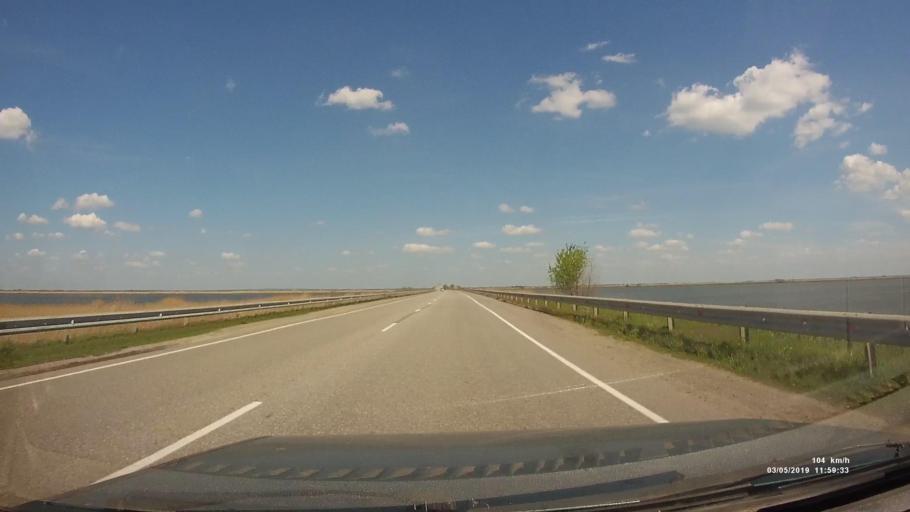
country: RU
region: Rostov
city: Bagayevskaya
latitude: 47.2366
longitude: 40.3315
